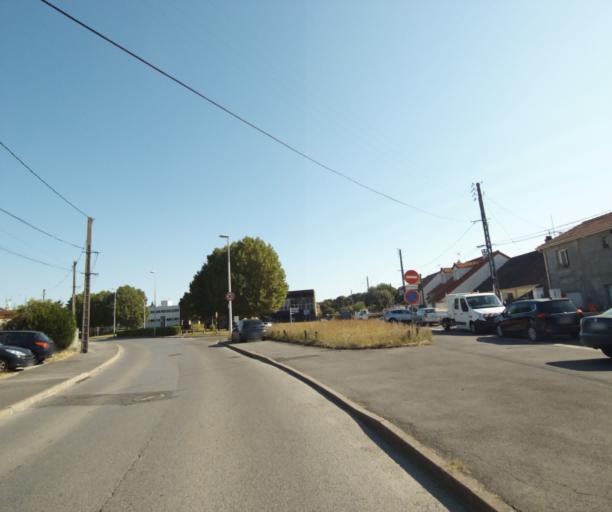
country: FR
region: Ile-de-France
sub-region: Departement de Seine-et-Marne
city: Lagny-sur-Marne
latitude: 48.8664
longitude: 2.7193
